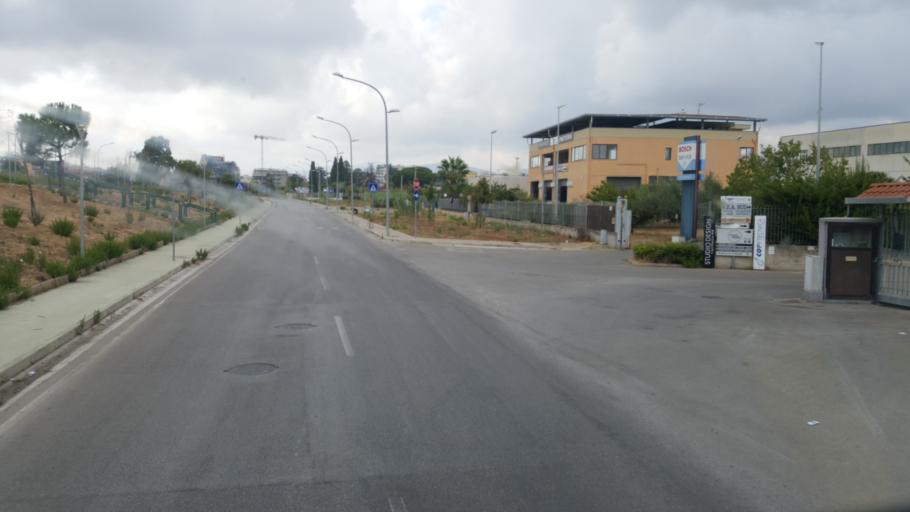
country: IT
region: Campania
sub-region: Provincia di Salerno
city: Battipaglia
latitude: 40.6003
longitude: 14.9860
